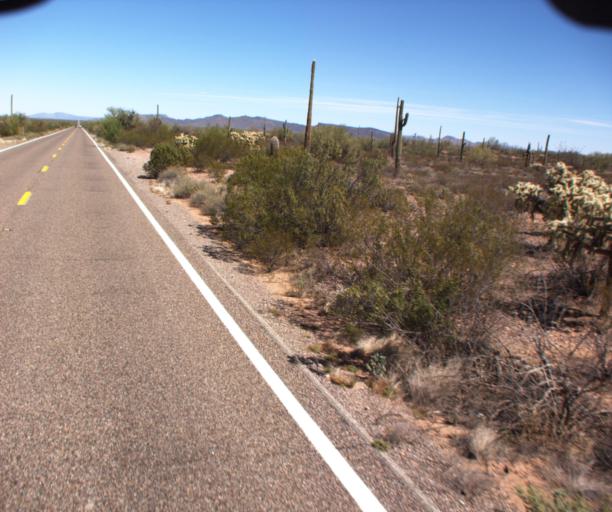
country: MX
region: Sonora
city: Sonoyta
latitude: 32.1119
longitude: -112.7698
